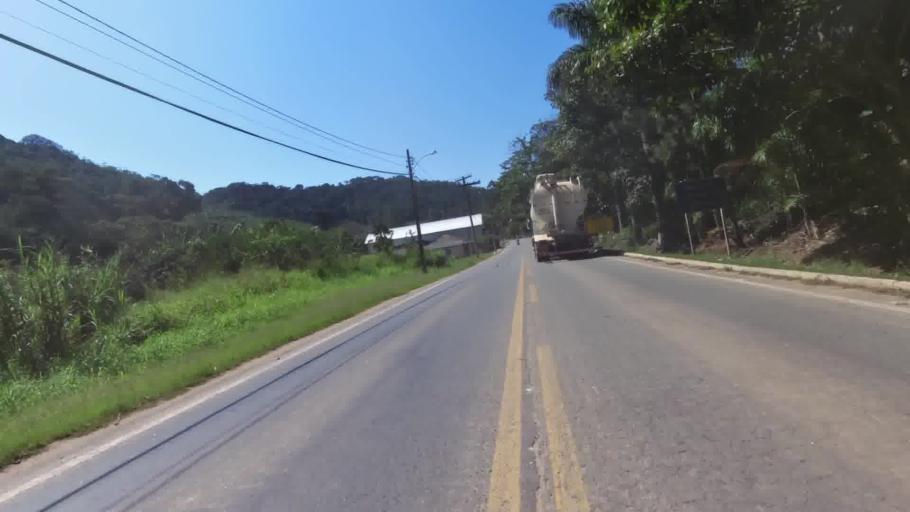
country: BR
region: Espirito Santo
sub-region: Marechal Floriano
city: Marechal Floriano
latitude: -20.4436
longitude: -40.7829
